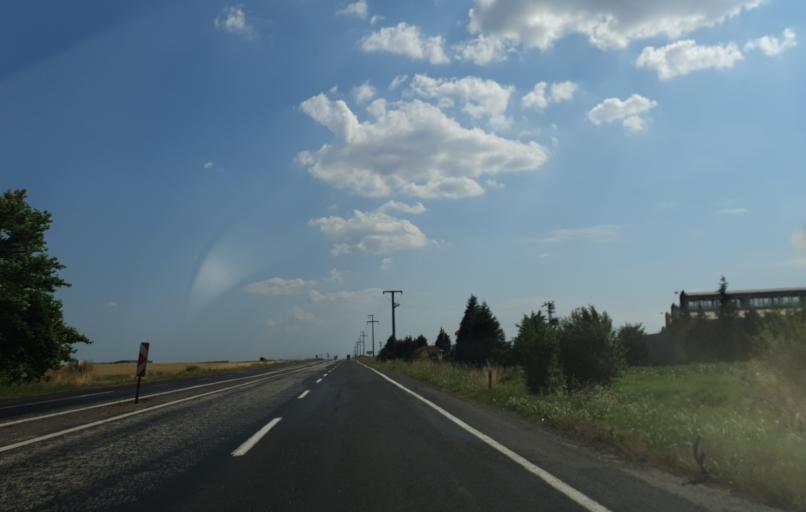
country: TR
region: Kirklareli
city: Buyukkaristiran
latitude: 41.2736
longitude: 27.5533
